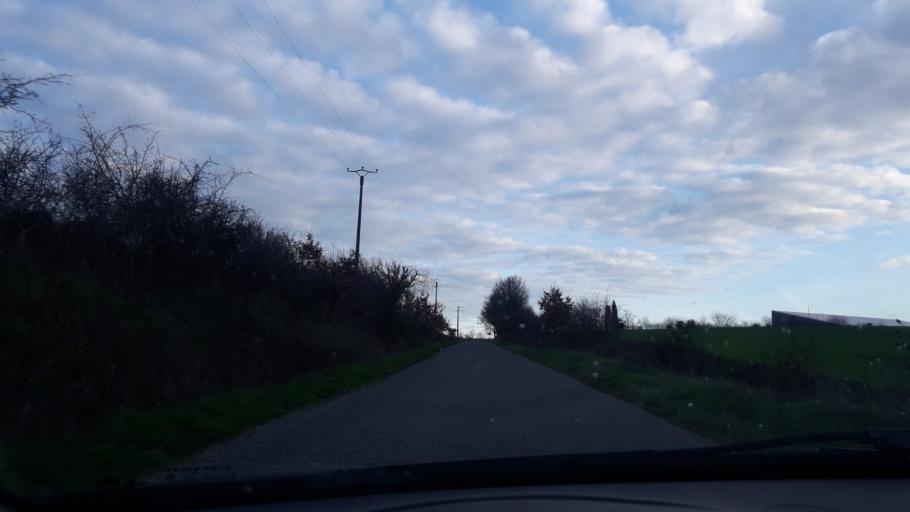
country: FR
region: Midi-Pyrenees
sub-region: Departement du Gers
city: Gimont
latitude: 43.6528
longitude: 1.0066
